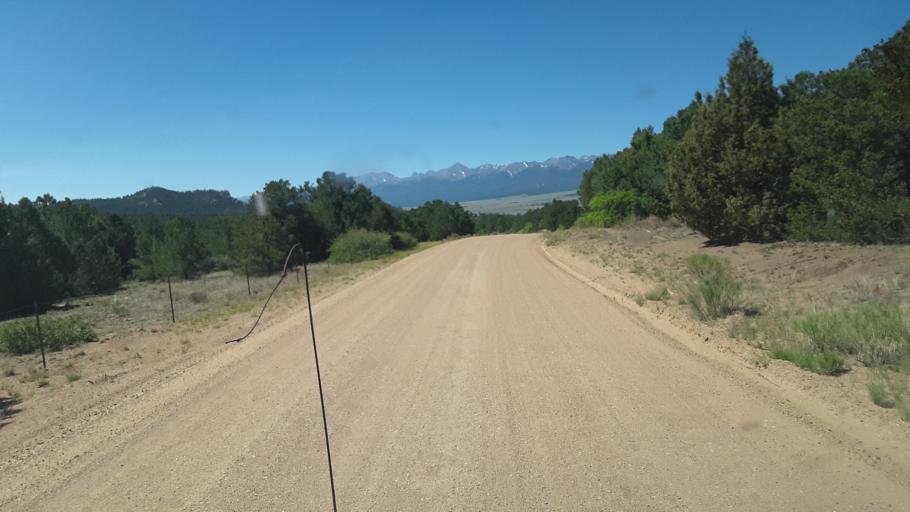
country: US
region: Colorado
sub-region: Custer County
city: Westcliffe
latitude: 38.2590
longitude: -105.5494
